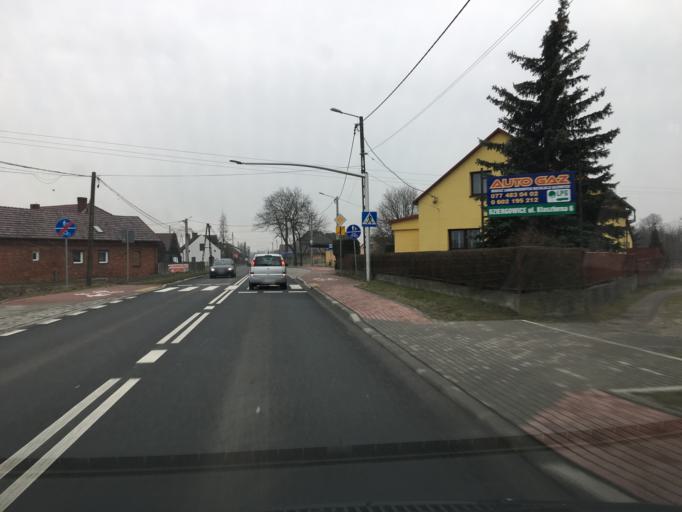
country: PL
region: Opole Voivodeship
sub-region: Powiat kedzierzynsko-kozielski
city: Kedzierzyn-Kozle
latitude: 50.3160
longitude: 18.2247
